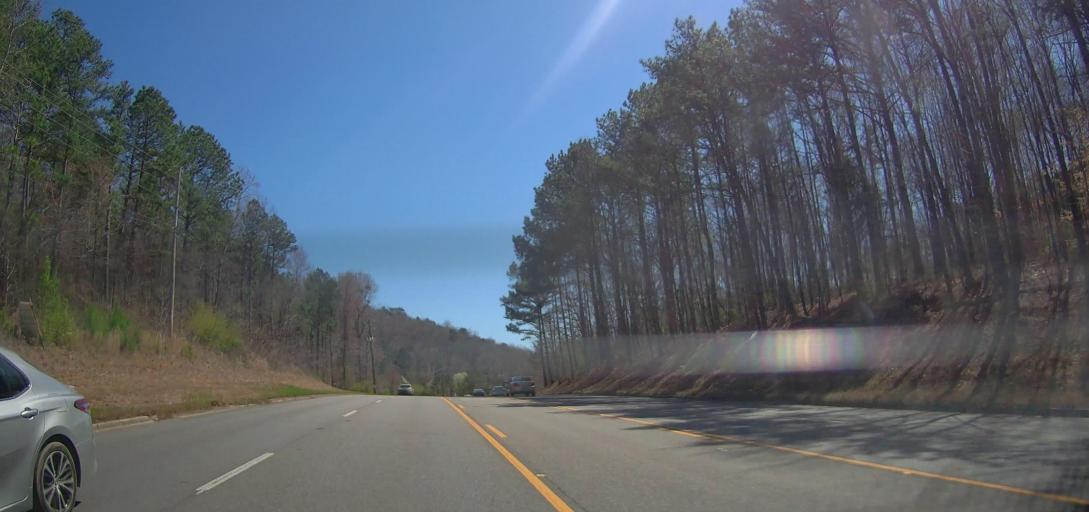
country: US
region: Alabama
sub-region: Etowah County
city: Rainbow City
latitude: 33.9506
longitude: -86.0334
